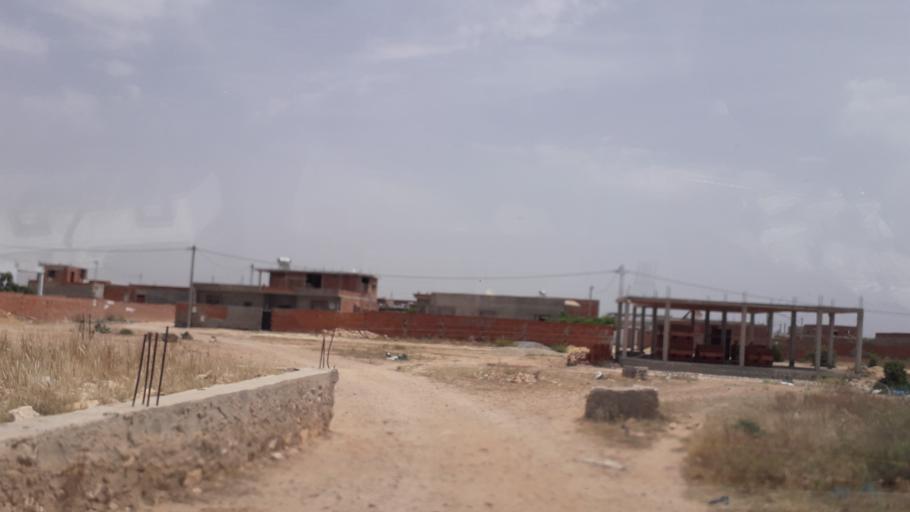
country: TN
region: Safaqis
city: Al Qarmadah
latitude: 34.8446
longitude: 10.7737
